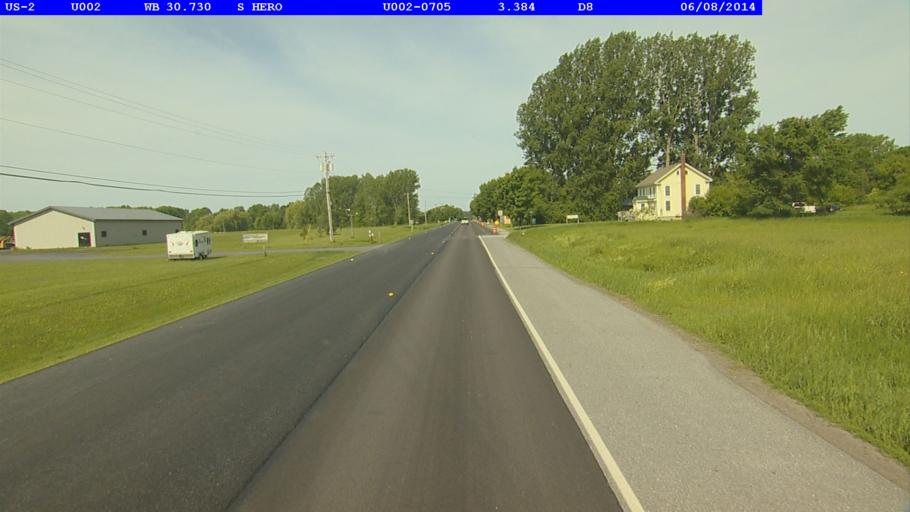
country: US
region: New York
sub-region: Clinton County
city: Cumberland Head
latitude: 44.6463
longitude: -73.2966
